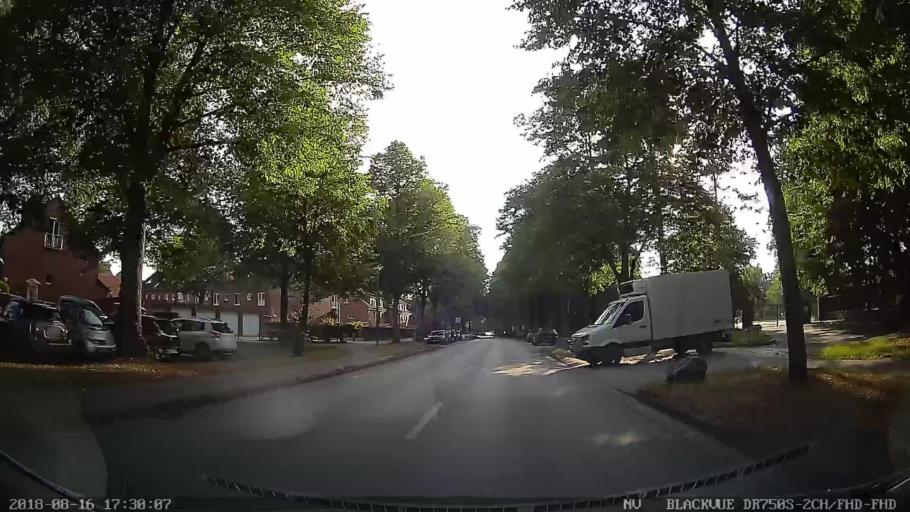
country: DE
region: Hamburg
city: Eidelstedt
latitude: 53.5777
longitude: 9.8614
